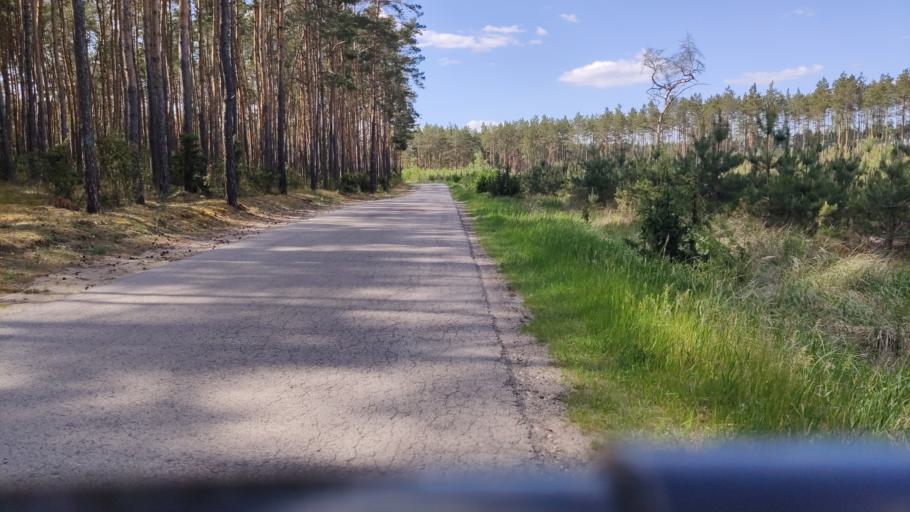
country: PL
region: Kujawsko-Pomorskie
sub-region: Wloclawek
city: Wloclawek
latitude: 52.5984
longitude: 19.0826
